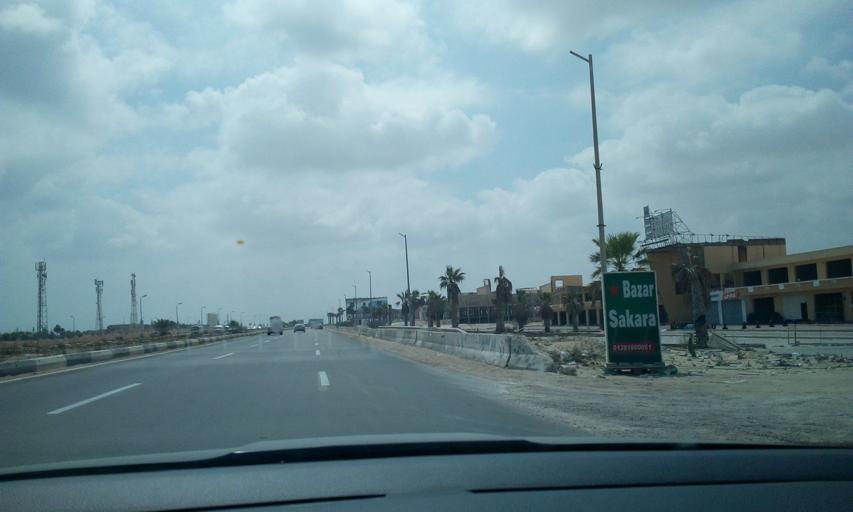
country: EG
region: Muhafazat Matruh
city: Al `Alamayn
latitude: 30.8315
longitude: 28.9672
